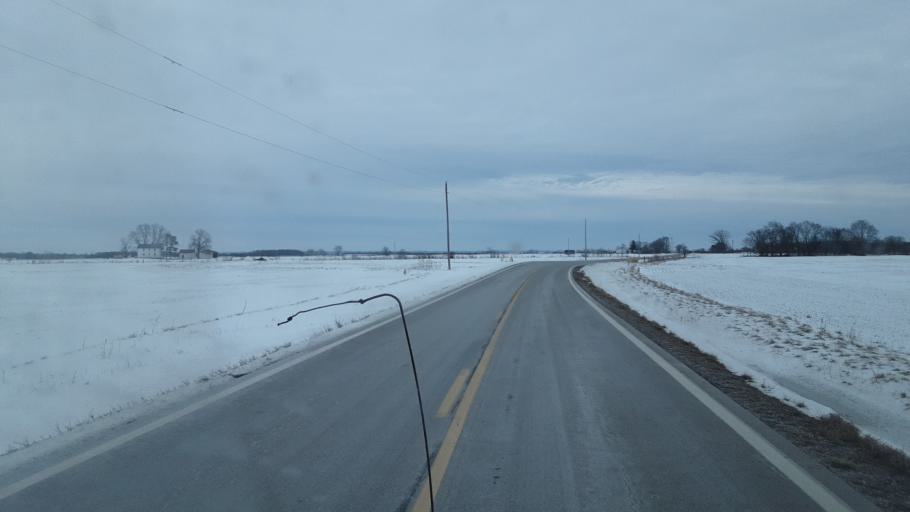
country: US
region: Ohio
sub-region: Pickaway County
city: Williamsport
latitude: 39.6378
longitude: -83.0800
